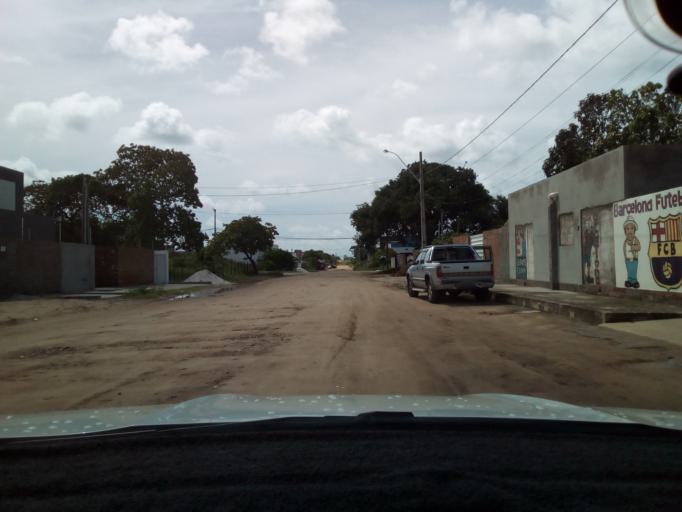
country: BR
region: Paraiba
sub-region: Joao Pessoa
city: Joao Pessoa
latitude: -7.1484
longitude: -34.8178
